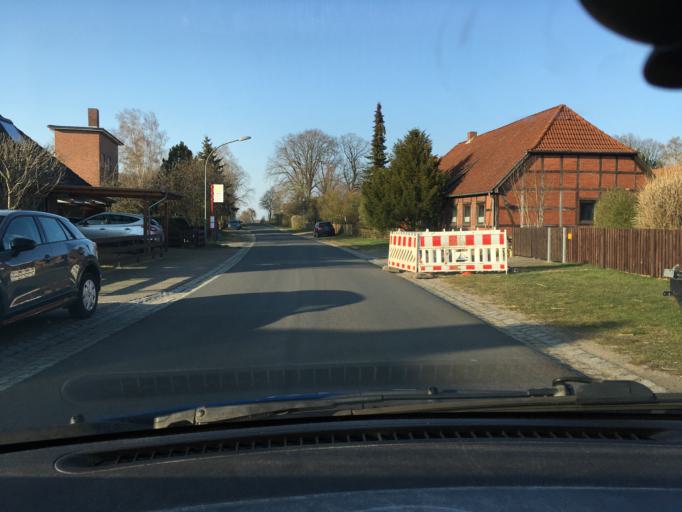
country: DE
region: Lower Saxony
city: Thomasburg
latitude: 53.2243
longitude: 10.6300
